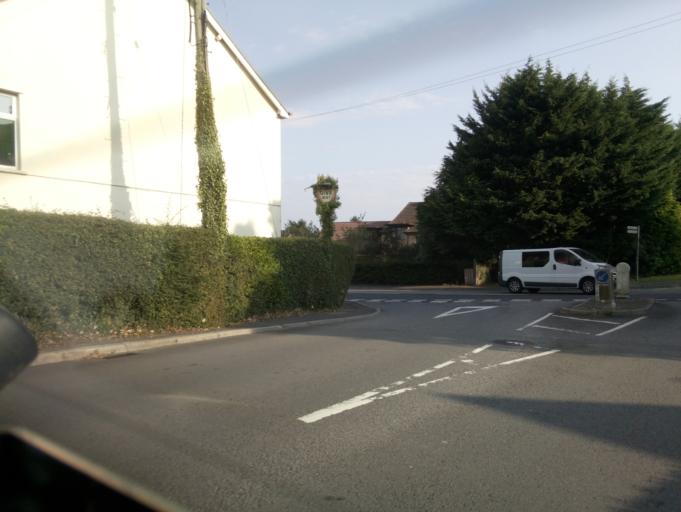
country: GB
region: Wales
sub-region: Torfaen County Borough
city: Cwmbran
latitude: 51.6664
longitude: -3.0262
